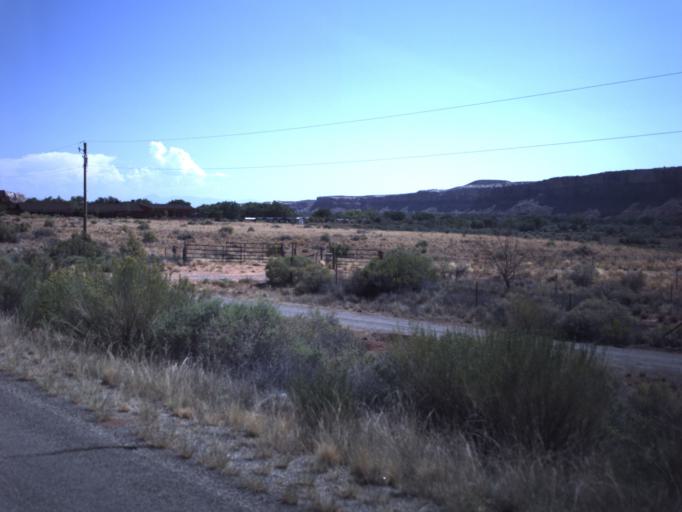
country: US
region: Utah
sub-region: San Juan County
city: Blanding
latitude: 37.2798
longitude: -109.5768
